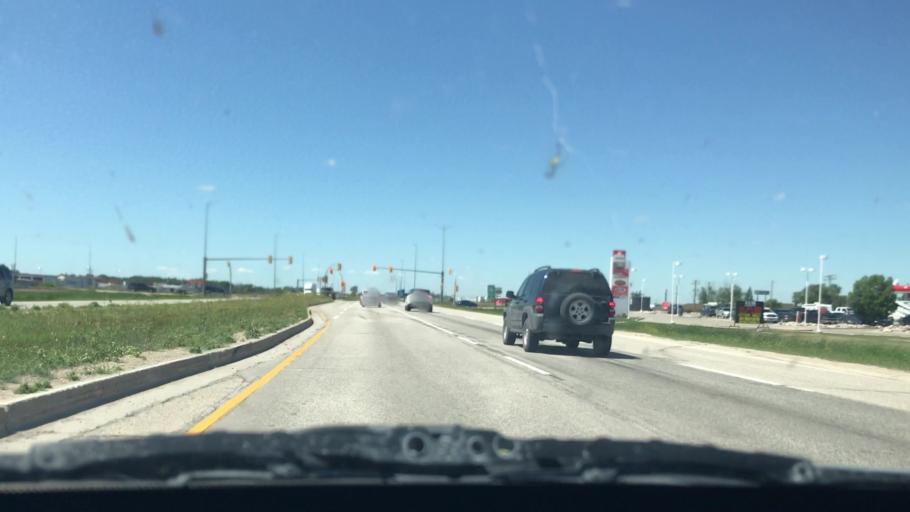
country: CA
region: Manitoba
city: Winnipeg
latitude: 49.8194
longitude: -96.9339
